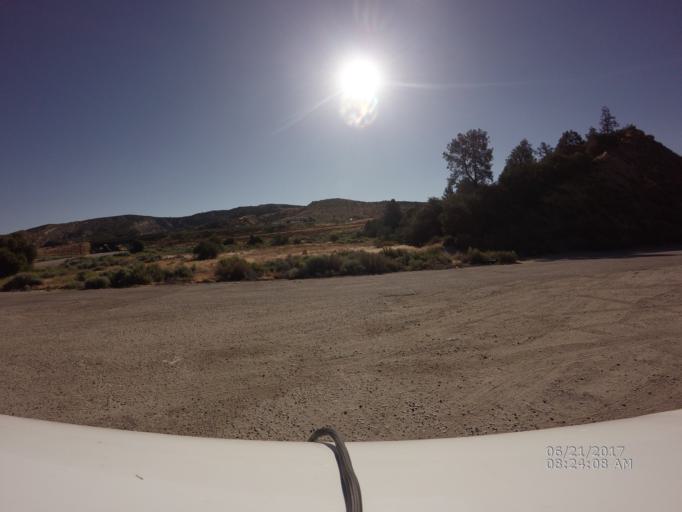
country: US
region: California
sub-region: Kern County
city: Lebec
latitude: 34.7062
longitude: -118.7978
